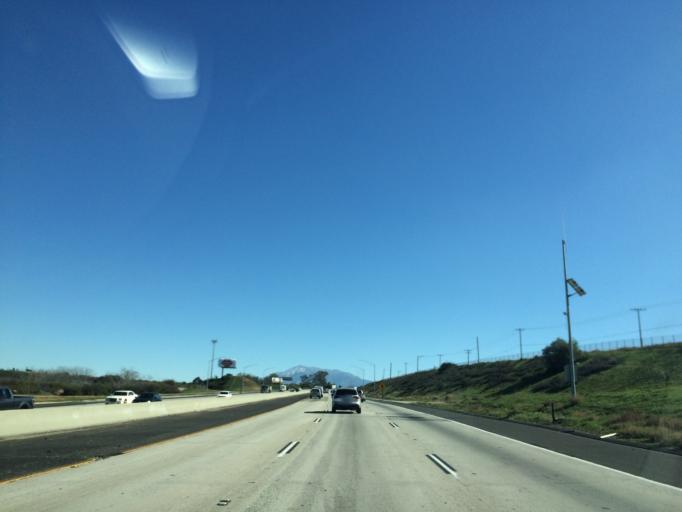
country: US
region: California
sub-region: Riverside County
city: Calimesa
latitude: 33.9679
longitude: -117.0355
